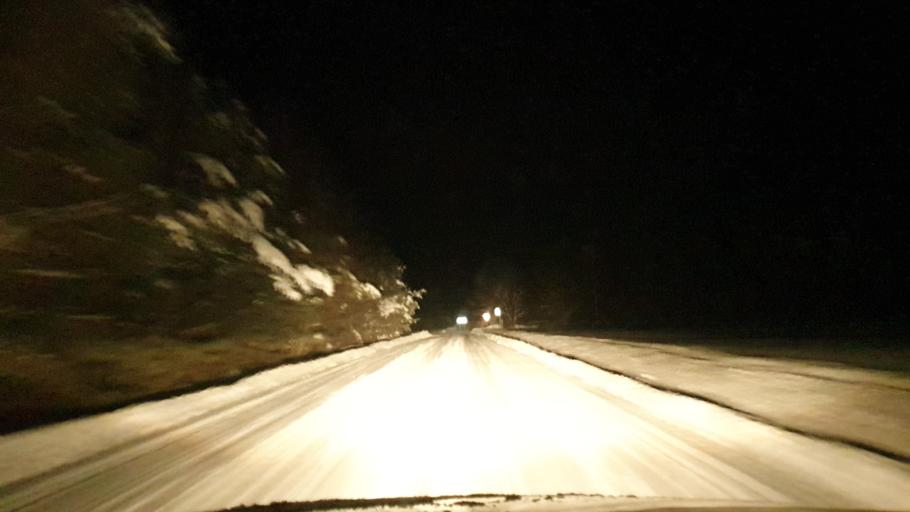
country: EE
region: Vorumaa
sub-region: Antsla vald
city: Vana-Antsla
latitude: 57.9563
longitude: 26.6596
